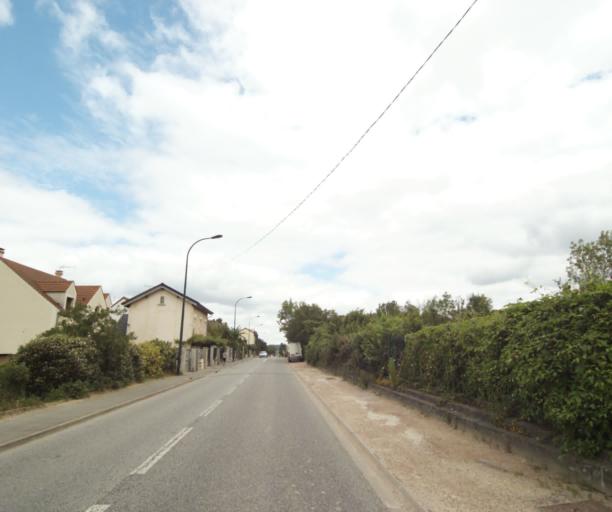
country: FR
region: Ile-de-France
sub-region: Departement des Yvelines
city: Saint-Cyr-l'Ecole
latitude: 48.8121
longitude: 2.0779
